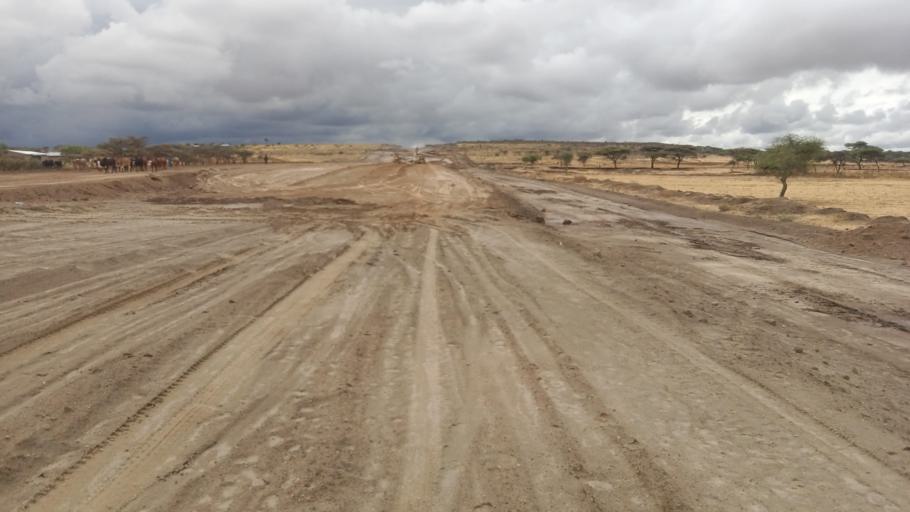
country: ET
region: Oromiya
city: Shashemene
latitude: 7.4905
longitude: 38.6806
